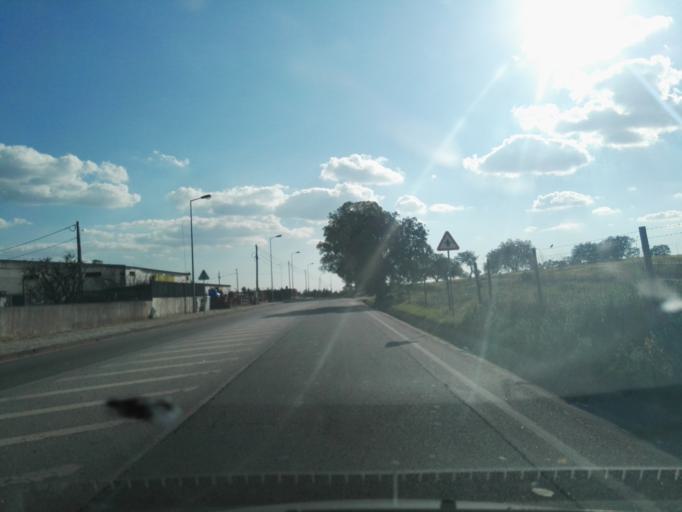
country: PT
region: Evora
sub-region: Evora
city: Evora
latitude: 38.5535
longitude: -7.9284
